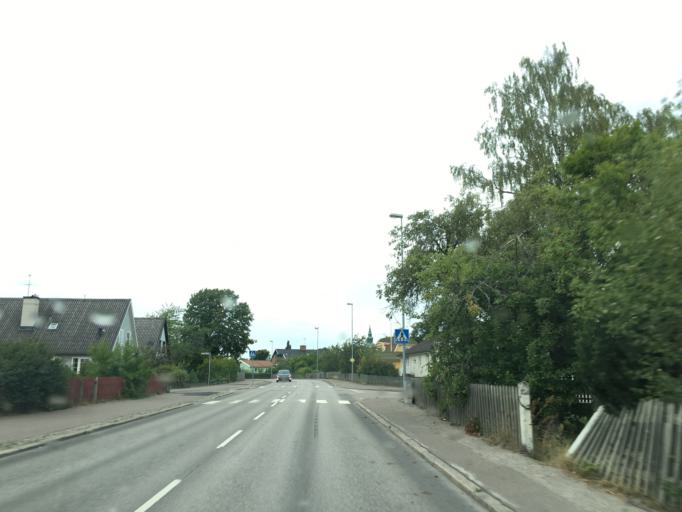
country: SE
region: Kalmar
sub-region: Nybro Kommun
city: Nybro
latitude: 56.7401
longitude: 15.9210
